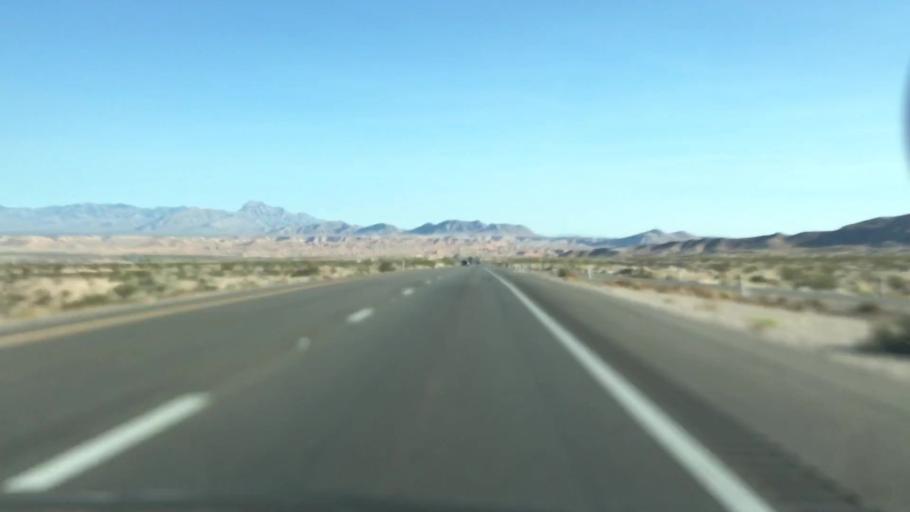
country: US
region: Nevada
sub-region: Clark County
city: Moapa Town
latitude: 36.6375
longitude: -114.5984
